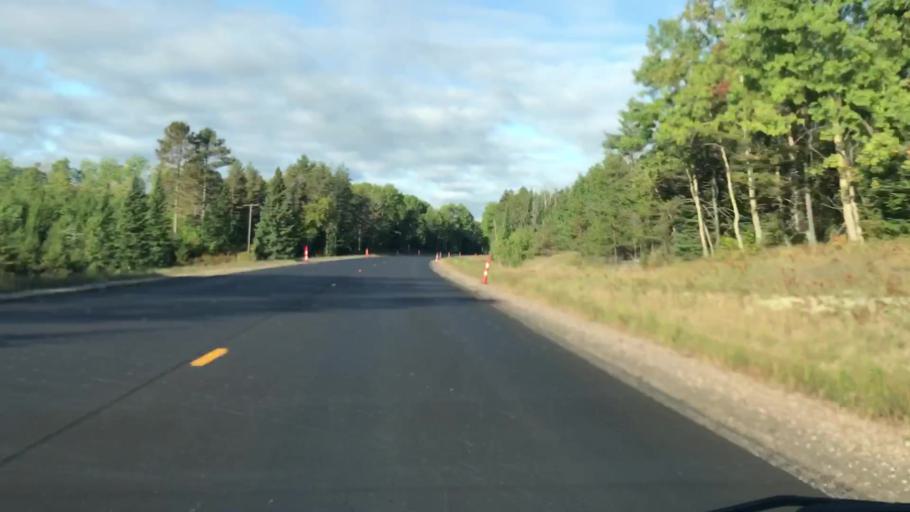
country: US
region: Michigan
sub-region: Mackinac County
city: Saint Ignace
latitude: 46.3465
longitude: -84.9200
